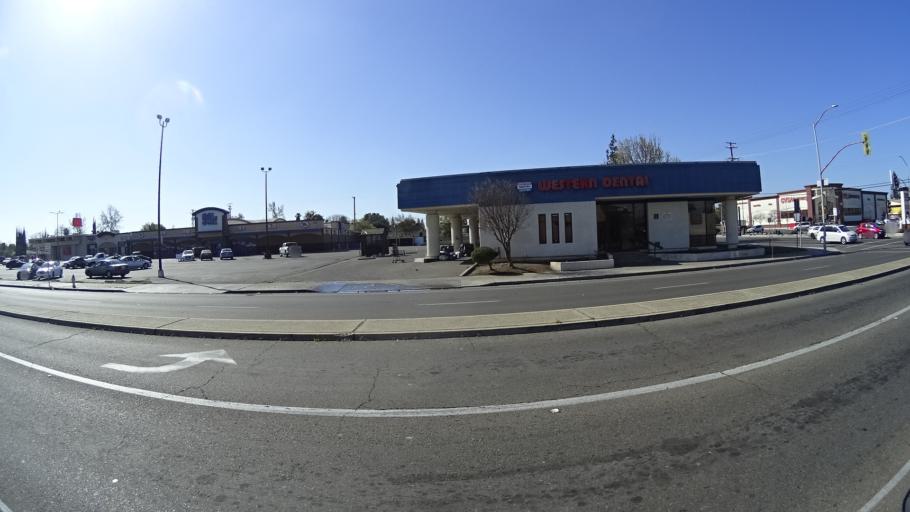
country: US
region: California
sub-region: Fresno County
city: Fresno
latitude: 36.7794
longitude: -119.8262
